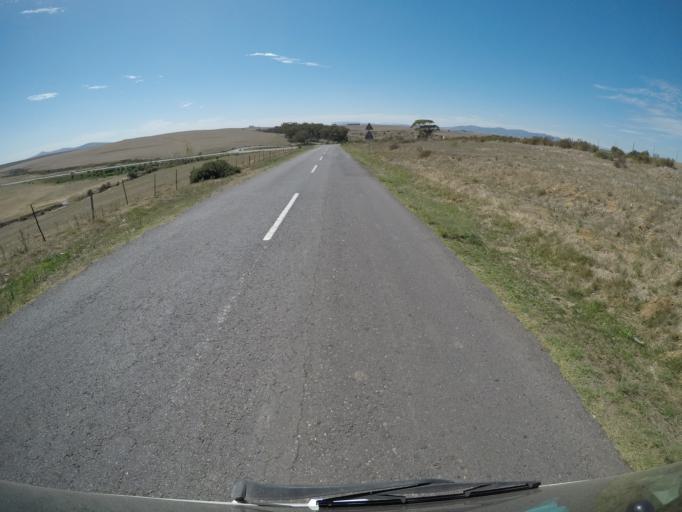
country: ZA
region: Western Cape
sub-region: City of Cape Town
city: Atlantis
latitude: -33.6800
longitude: 18.6033
